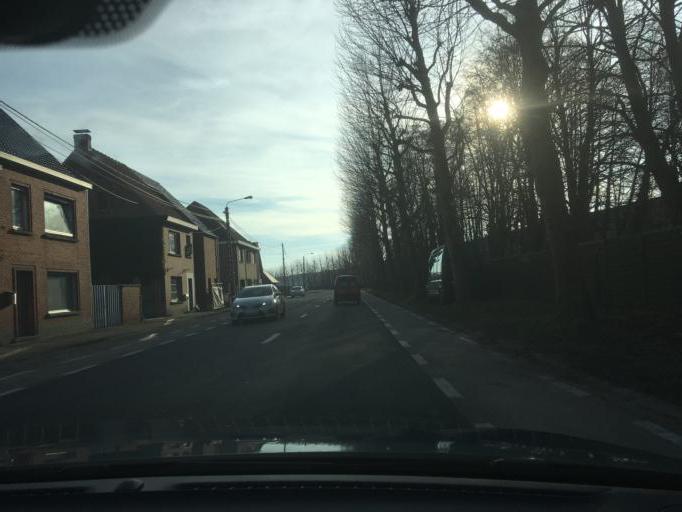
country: BE
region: Flanders
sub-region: Provincie West-Vlaanderen
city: Wielsbeke
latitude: 50.9198
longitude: 3.3727
